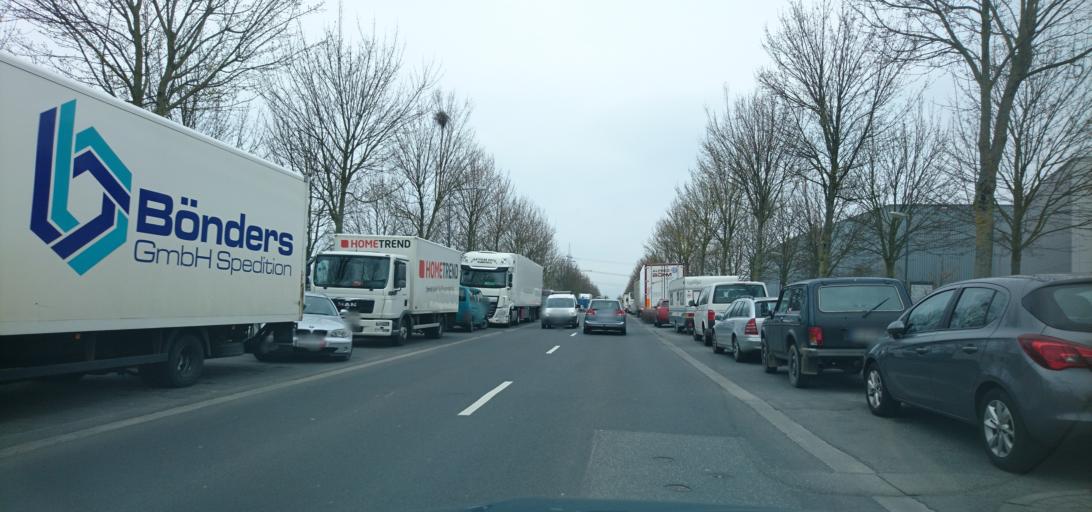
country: DE
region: Hesse
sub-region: Regierungsbezirk Darmstadt
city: Bad Homburg vor der Hoehe
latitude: 50.1934
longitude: 8.6462
